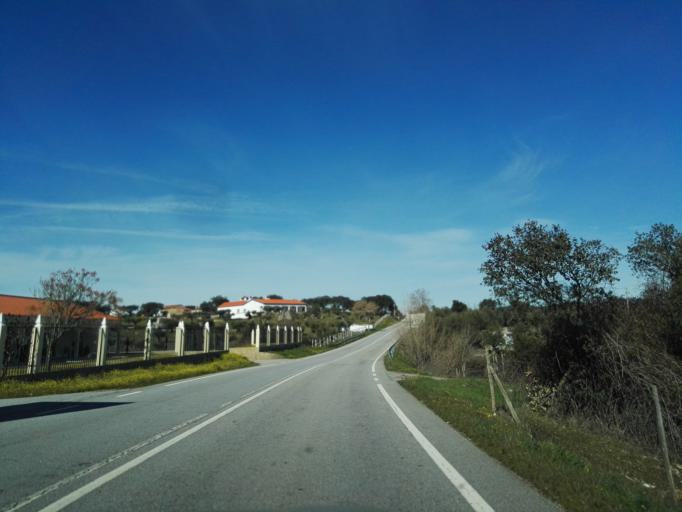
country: PT
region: Portalegre
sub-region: Arronches
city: Arronches
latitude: 39.1207
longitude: -7.2951
